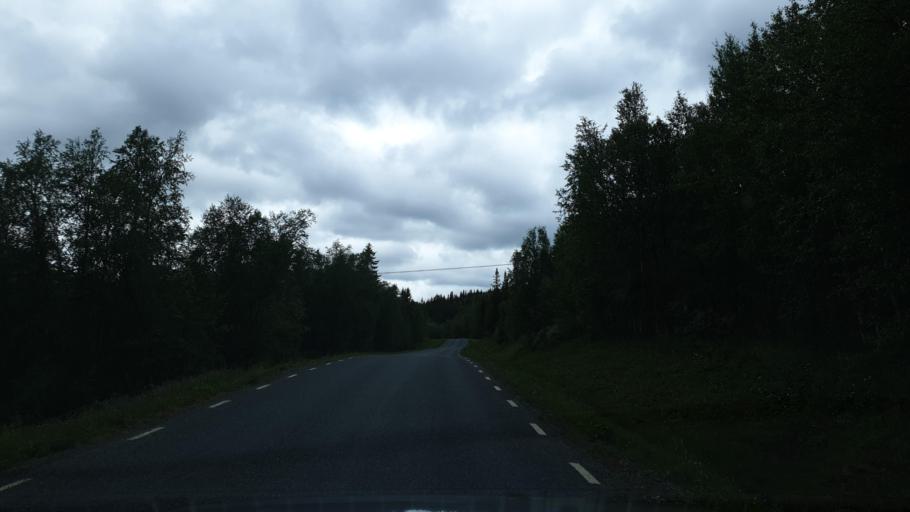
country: SE
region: Vaesterbotten
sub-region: Vilhelmina Kommun
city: Sjoberg
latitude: 65.2781
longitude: 15.3153
